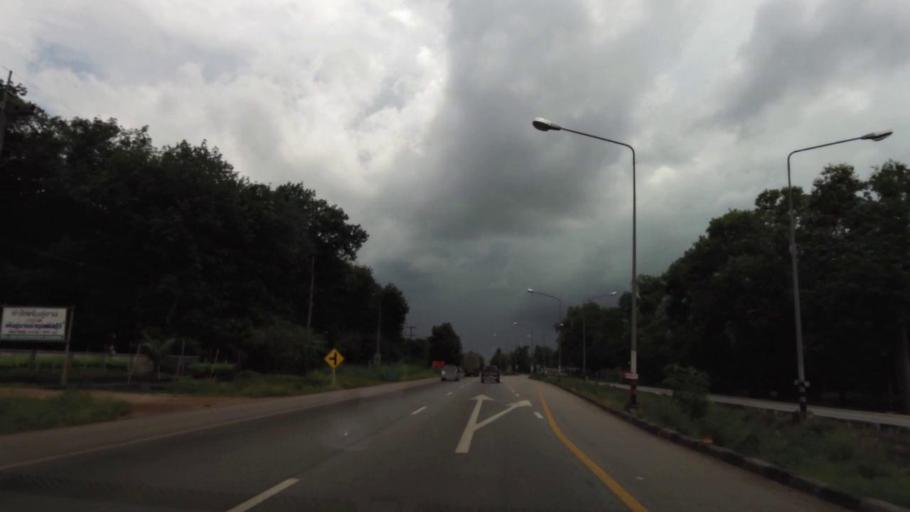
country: TH
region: Rayong
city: Wang Chan
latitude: 12.9132
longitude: 101.5335
